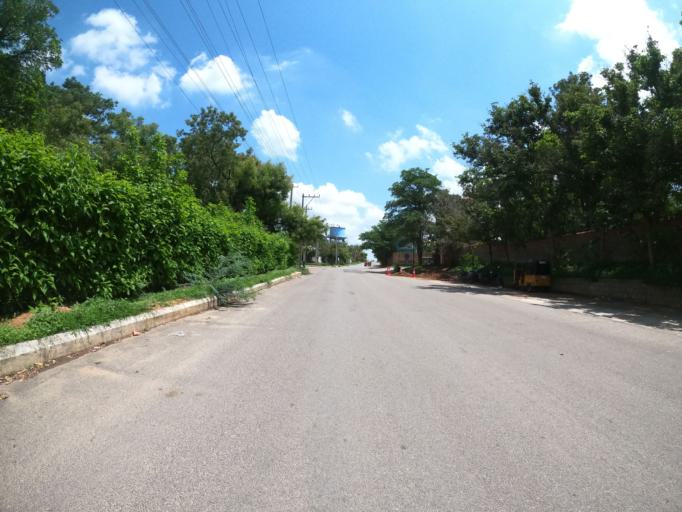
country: IN
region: Telangana
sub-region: Medak
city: Serilingampalle
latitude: 17.3891
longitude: 78.3152
